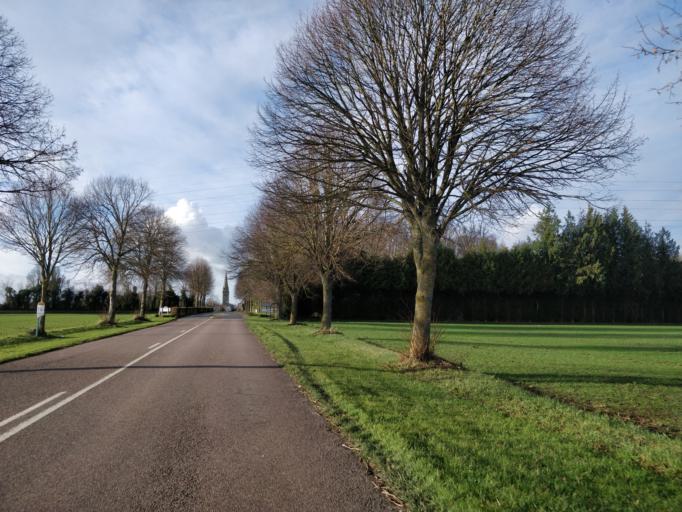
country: FR
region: Lower Normandy
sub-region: Departement du Calvados
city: Saint-Manvieu-Norrey
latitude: 49.2074
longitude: -0.5025
